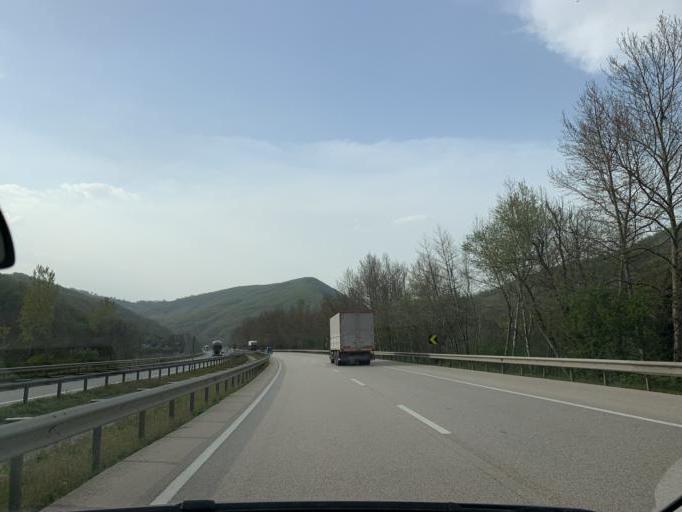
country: TR
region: Bursa
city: Tahtakopru
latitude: 39.9847
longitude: 29.6571
